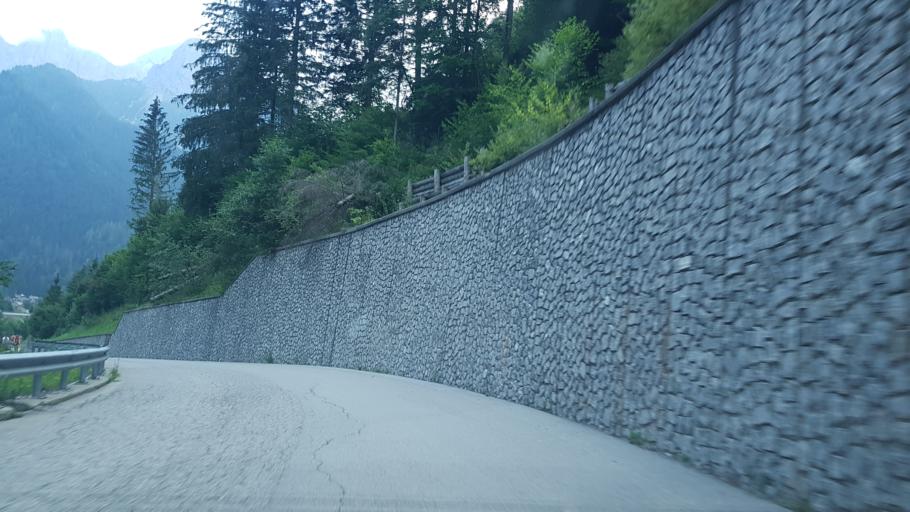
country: IT
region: Friuli Venezia Giulia
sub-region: Provincia di Udine
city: Forni Avoltri
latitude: 46.5947
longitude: 12.7752
